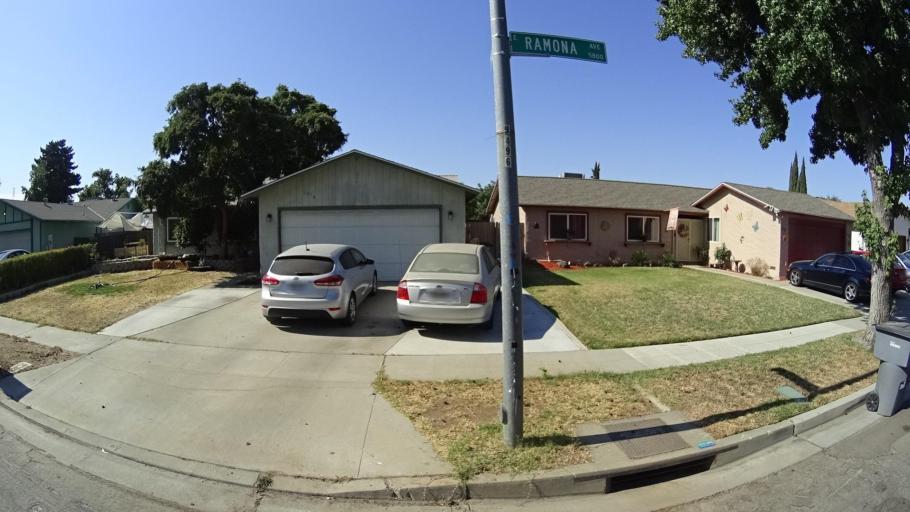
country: US
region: California
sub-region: Fresno County
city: Tarpey Village
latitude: 36.7852
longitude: -119.6880
